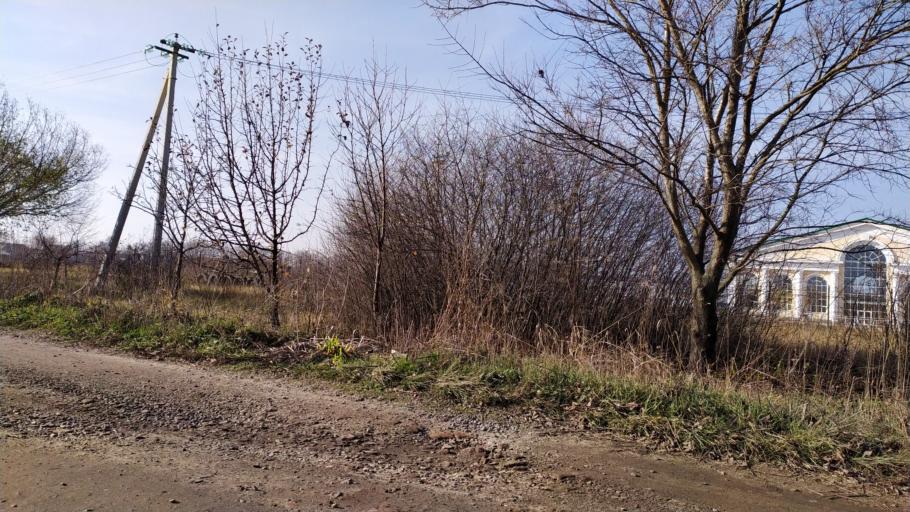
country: RU
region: Kursk
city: Kursk
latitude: 51.6412
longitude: 36.1309
